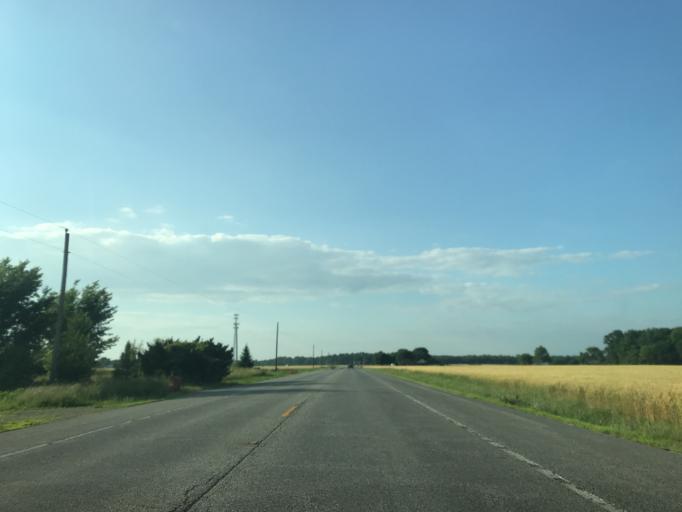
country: US
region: Maryland
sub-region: Caroline County
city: Denton
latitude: 38.8303
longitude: -75.7780
